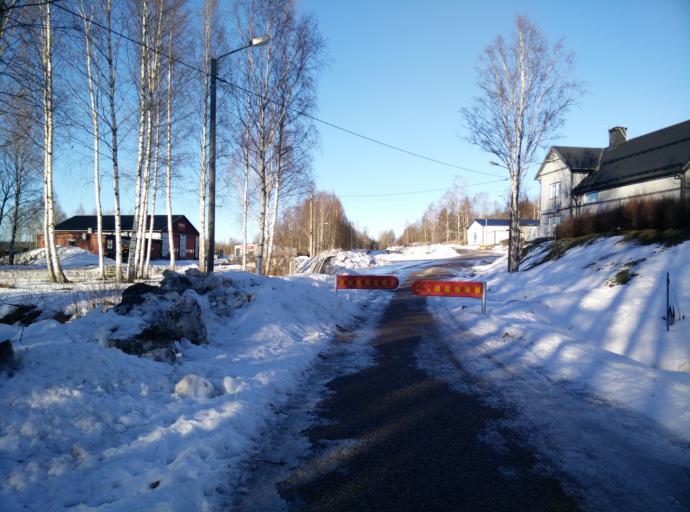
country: SE
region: Vaesternorrland
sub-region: Sundsvalls Kommun
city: Skottsund
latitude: 62.3117
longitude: 17.3927
